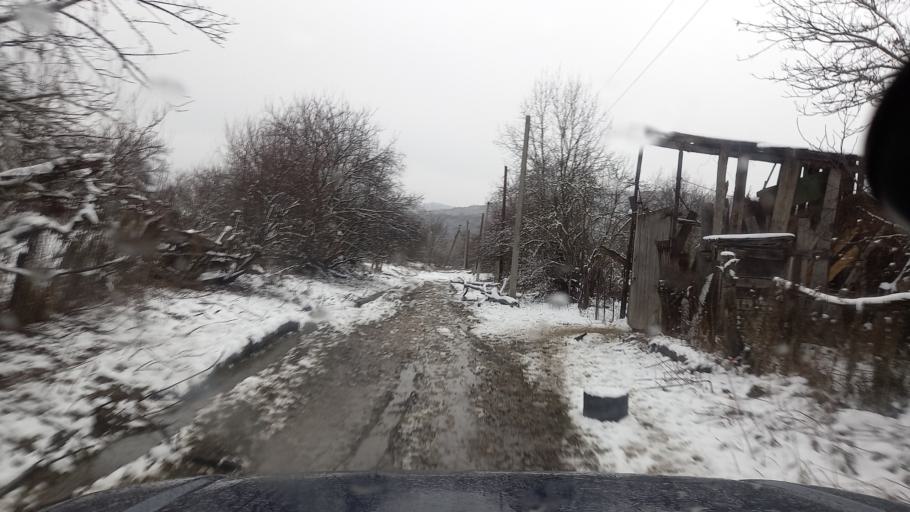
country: RU
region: Adygeya
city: Abadzekhskaya
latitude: 44.3545
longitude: 40.4163
